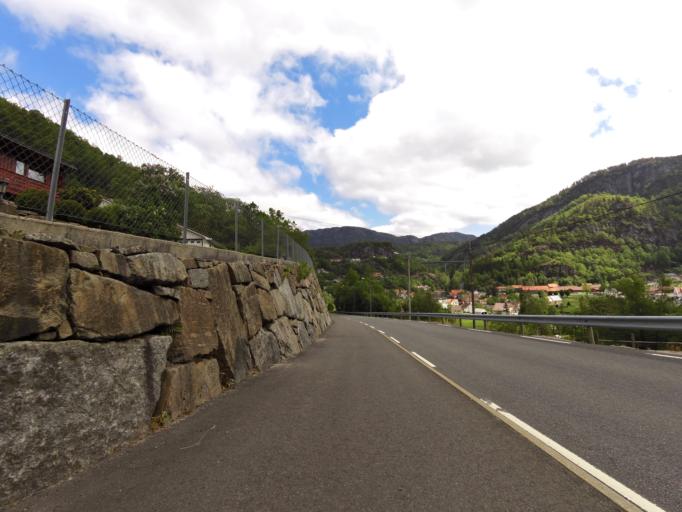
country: NO
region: Vest-Agder
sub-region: Flekkefjord
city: Flekkefjord
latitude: 58.2691
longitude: 6.8095
